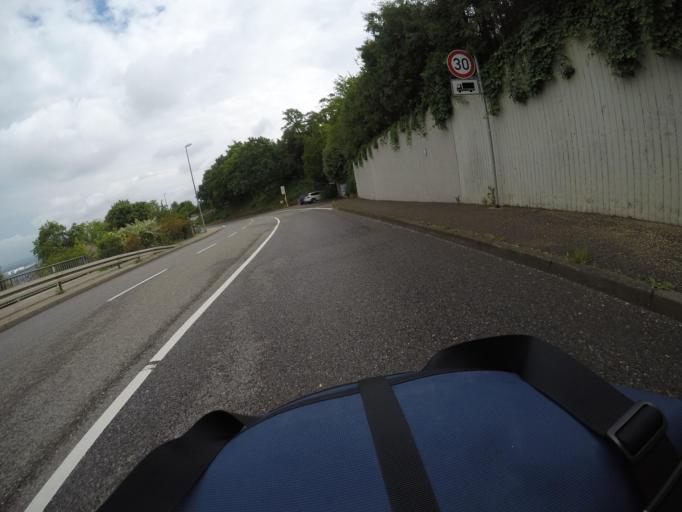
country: DE
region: Baden-Wuerttemberg
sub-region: Regierungsbezirk Stuttgart
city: Gerlingen
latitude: 48.7907
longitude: 9.0634
